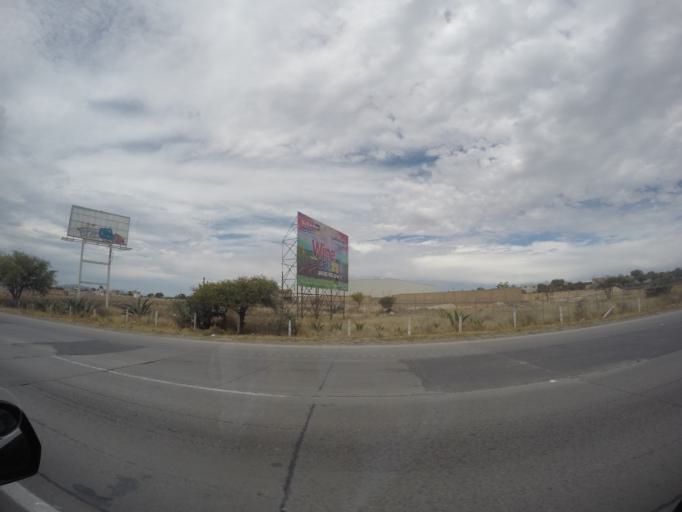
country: MX
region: Queretaro
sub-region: San Juan del Rio
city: Paso de Mata
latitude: 20.3501
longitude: -99.9525
